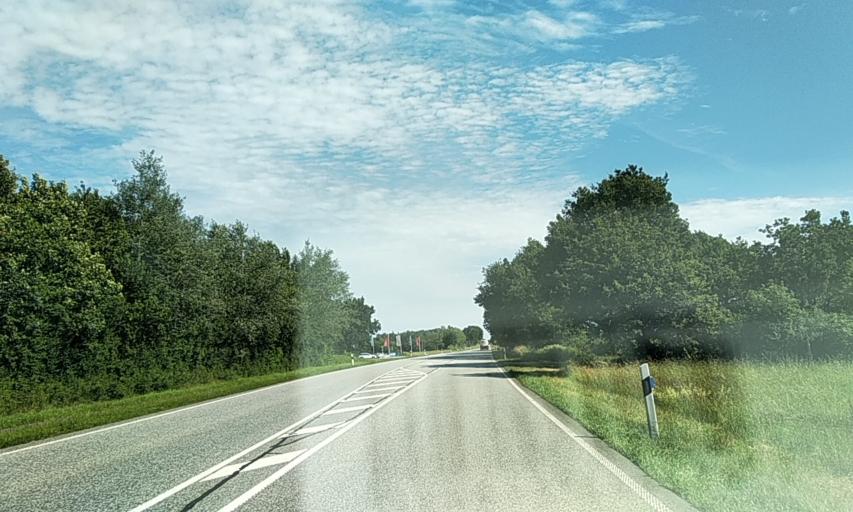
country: DE
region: Schleswig-Holstein
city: Kropp
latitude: 54.4174
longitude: 9.5297
